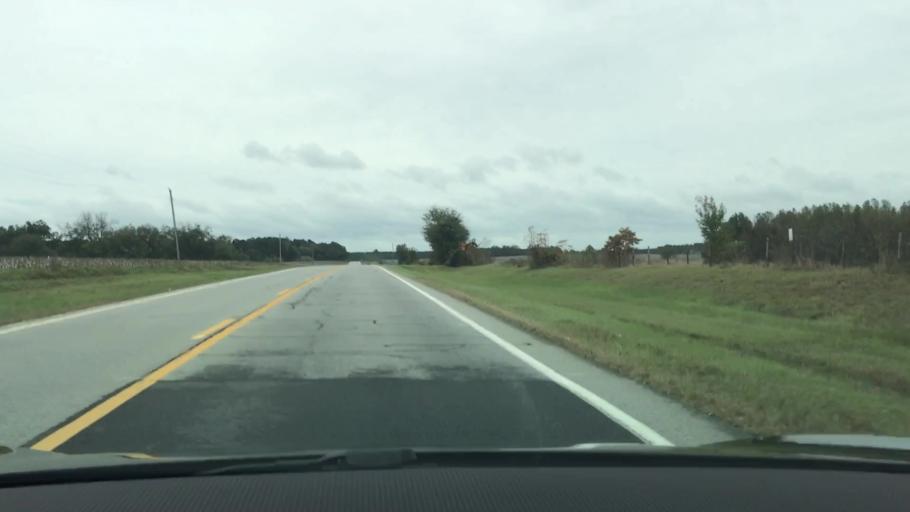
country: US
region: Georgia
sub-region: Warren County
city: Warrenton
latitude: 33.3679
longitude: -82.6000
